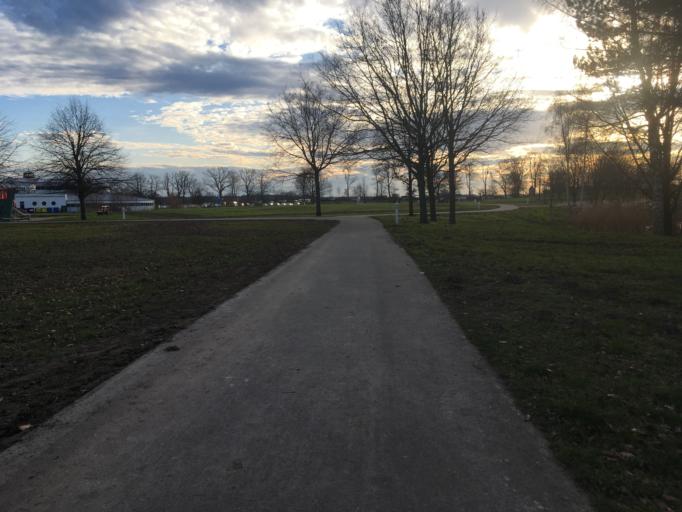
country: DE
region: Mecklenburg-Vorpommern
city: Ostseebad Sellin
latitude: 54.3745
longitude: 13.6941
